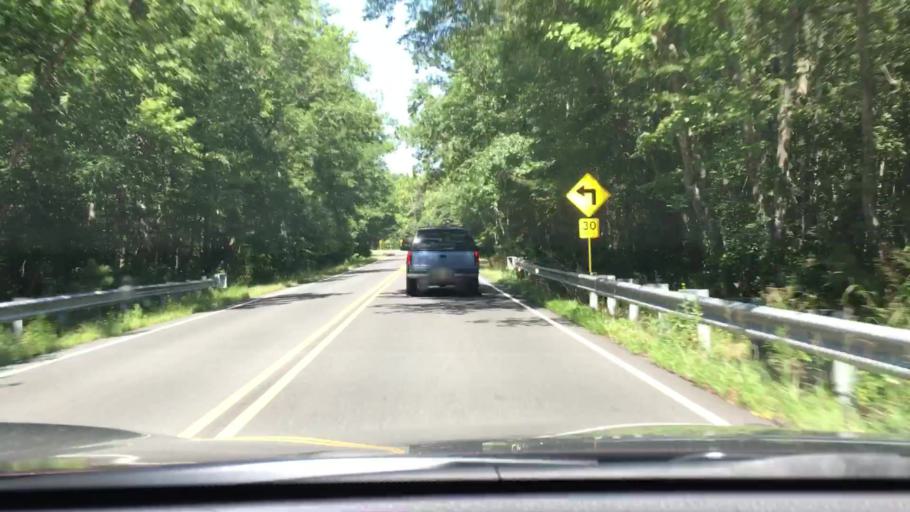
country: US
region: New Jersey
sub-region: Cape May County
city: Woodbine
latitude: 39.2604
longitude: -74.9124
